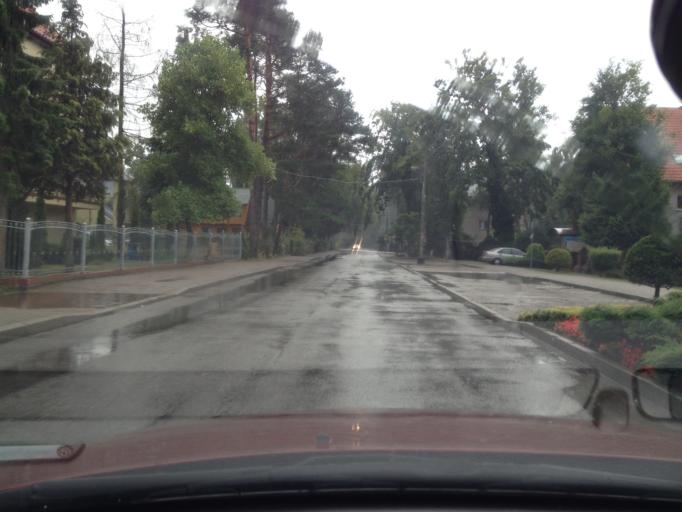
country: PL
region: West Pomeranian Voivodeship
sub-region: Powiat gryficki
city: Pobierowo
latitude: 54.0567
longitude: 14.9281
